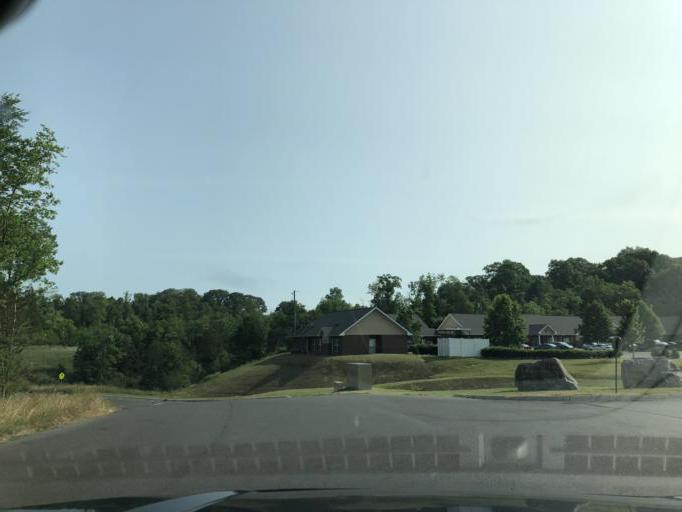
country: US
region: Tennessee
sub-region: Rutherford County
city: La Vergne
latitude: 36.0487
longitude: -86.6379
